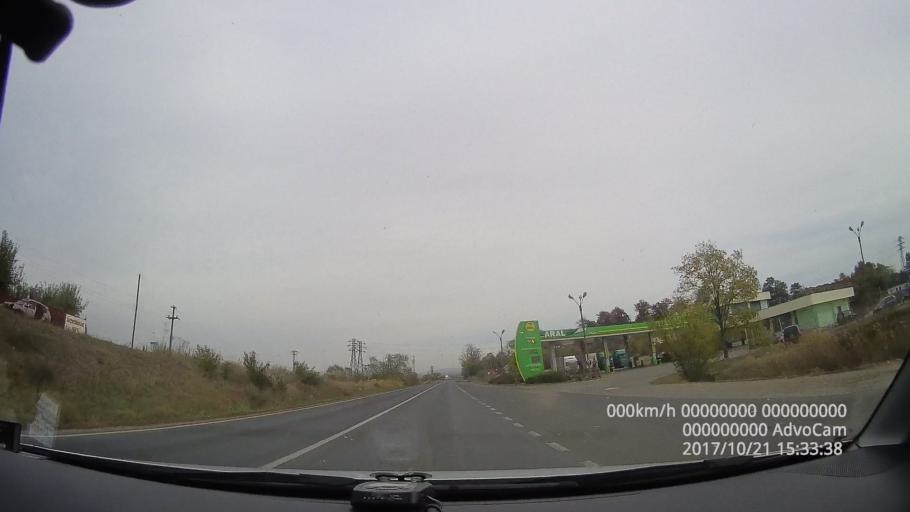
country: RO
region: Hunedoara
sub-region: Comuna Soimus
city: Soimus
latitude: 45.9066
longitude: 22.8759
